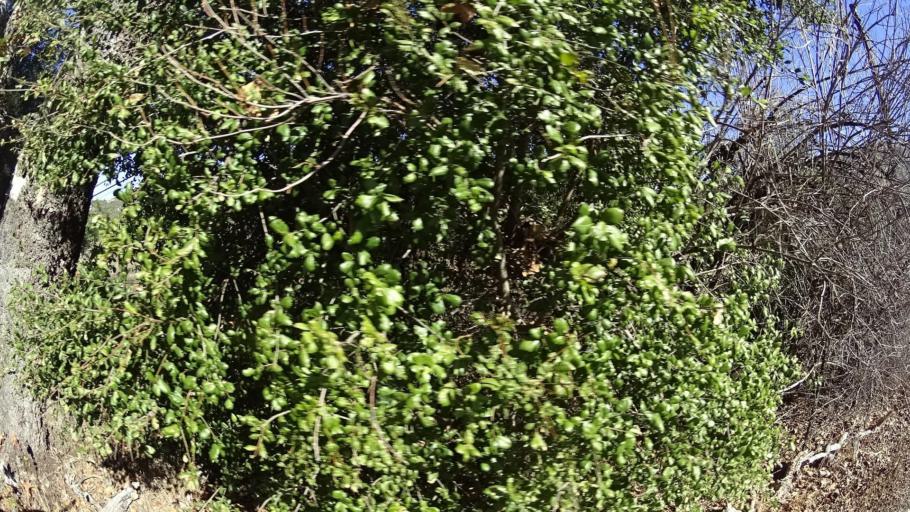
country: US
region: California
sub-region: San Diego County
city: Jamul
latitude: 32.7138
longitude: -116.7599
